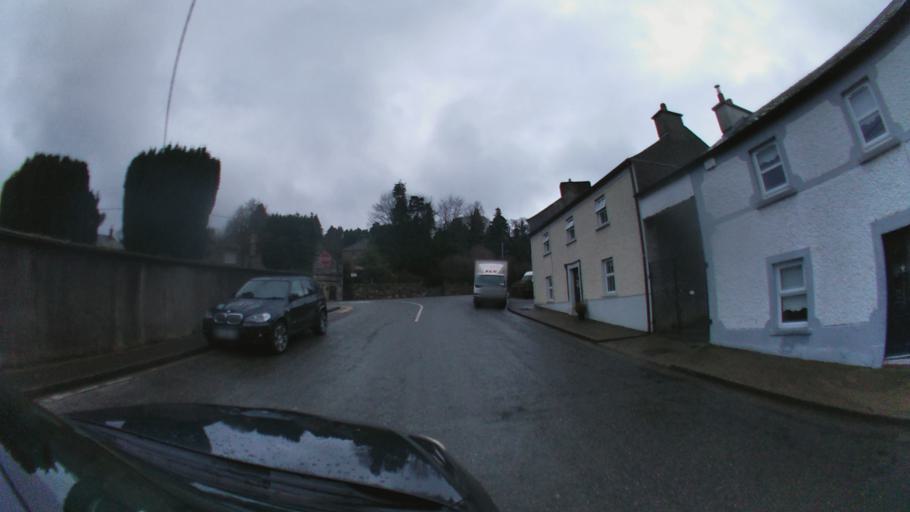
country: IE
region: Leinster
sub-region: Kilkenny
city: Graiguenamanagh
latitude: 52.5412
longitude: -6.9536
